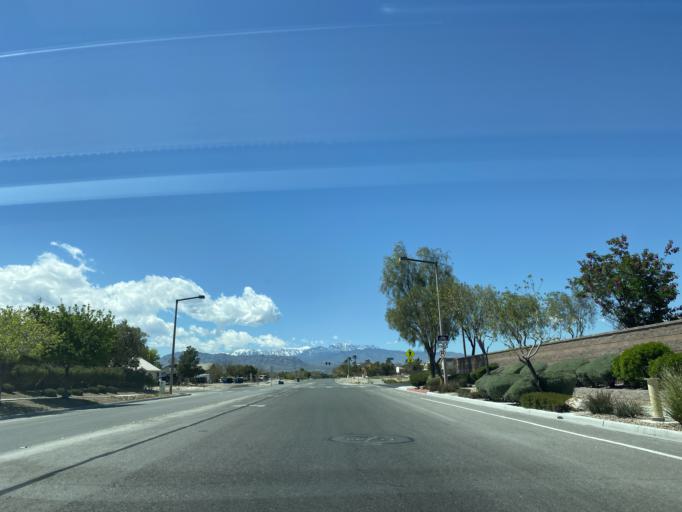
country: US
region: Nevada
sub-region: Clark County
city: North Las Vegas
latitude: 36.3132
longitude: -115.2127
